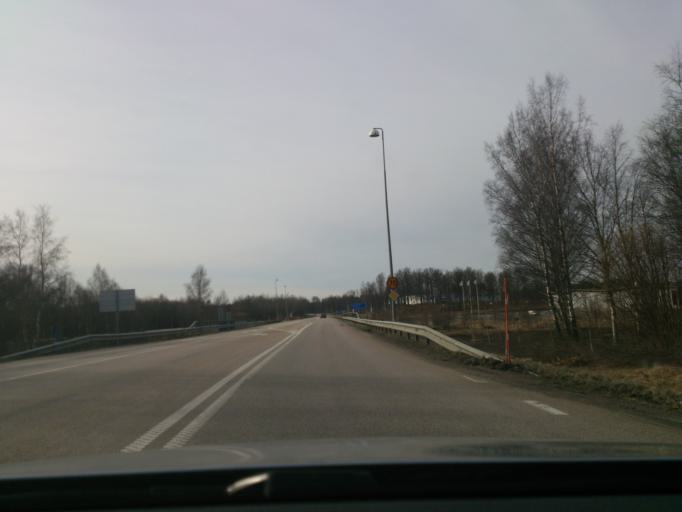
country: SE
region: Kronoberg
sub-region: Alvesta Kommun
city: Alvesta
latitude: 56.9232
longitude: 14.5587
